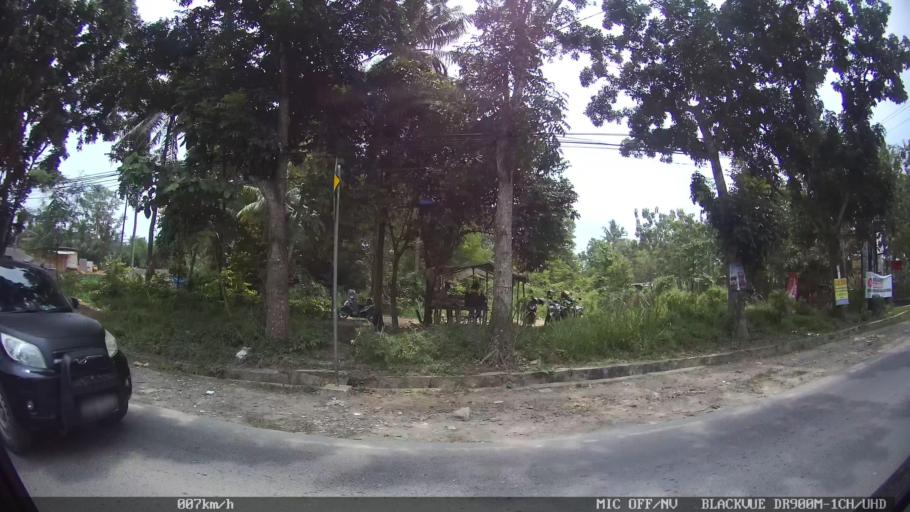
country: ID
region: Lampung
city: Kedaton
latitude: -5.4027
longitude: 105.3156
